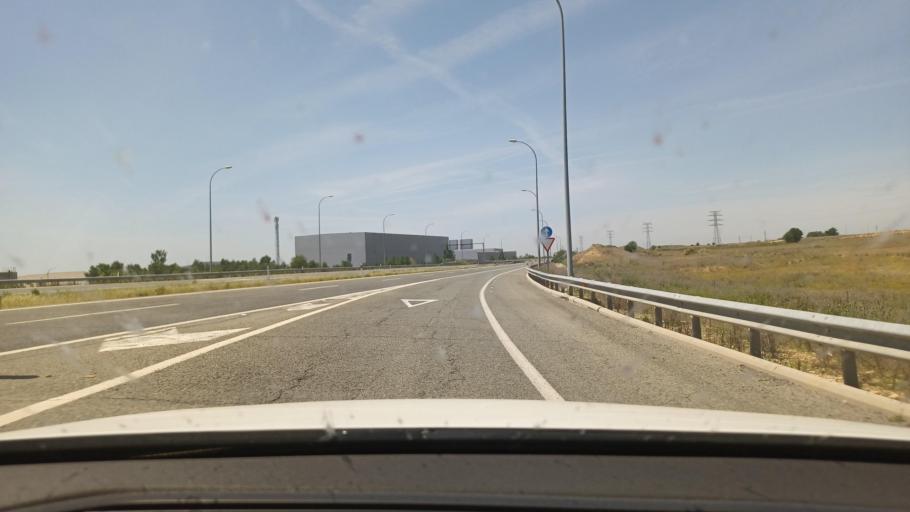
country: ES
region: Madrid
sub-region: Provincia de Madrid
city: Meco
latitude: 40.5365
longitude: -3.3176
